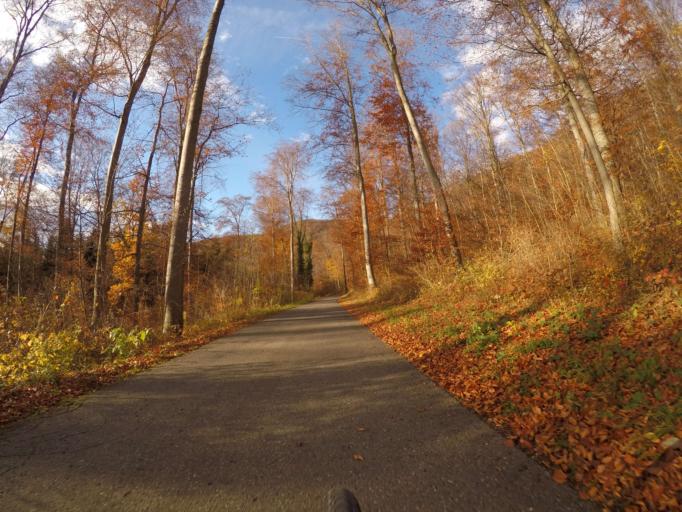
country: DE
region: Baden-Wuerttemberg
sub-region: Tuebingen Region
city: Eningen unter Achalm
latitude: 48.4718
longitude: 9.2897
